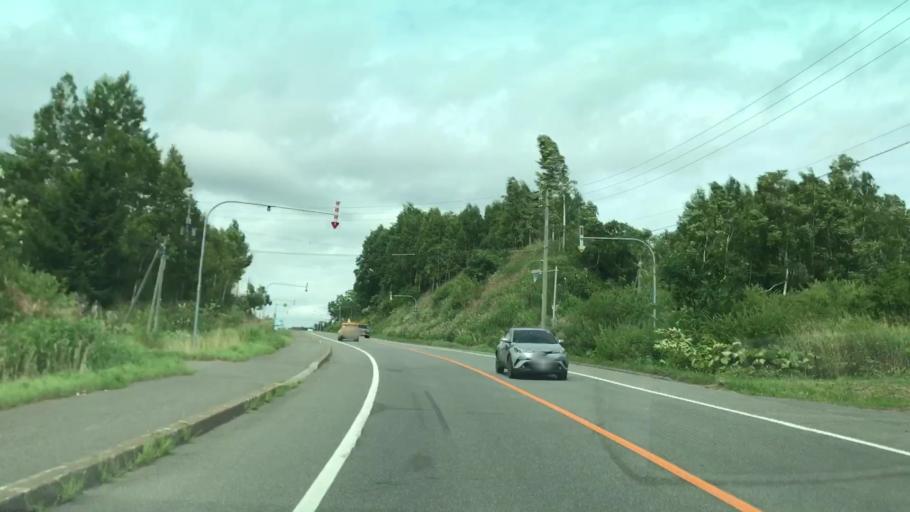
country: JP
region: Hokkaido
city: Niseko Town
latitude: 42.9124
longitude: 140.7527
